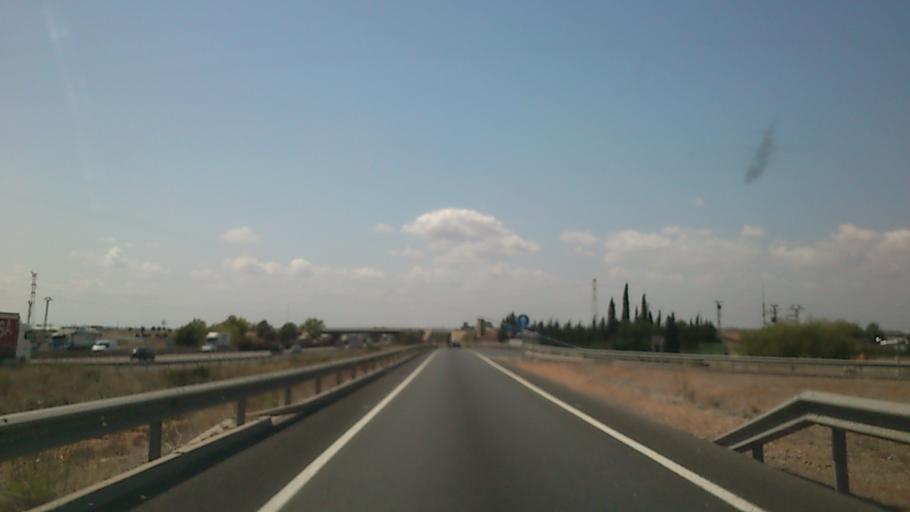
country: ES
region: Valencia
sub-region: Provincia de Valencia
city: Museros
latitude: 39.5916
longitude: -0.3780
